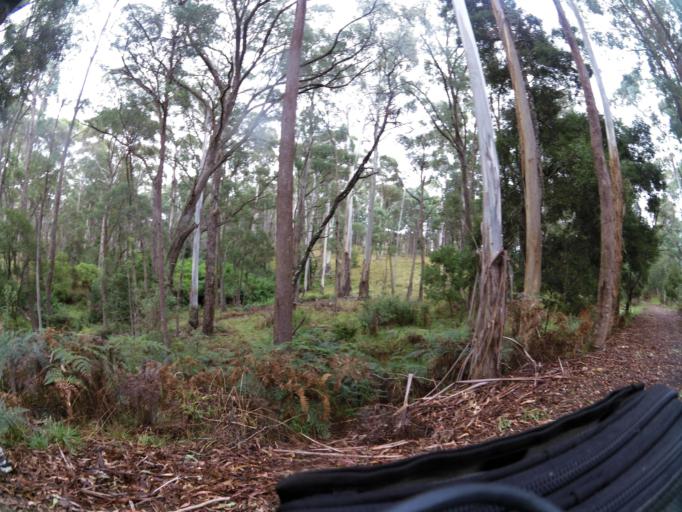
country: AU
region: New South Wales
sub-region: Greater Hume Shire
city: Holbrook
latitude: -36.1608
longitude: 147.4867
